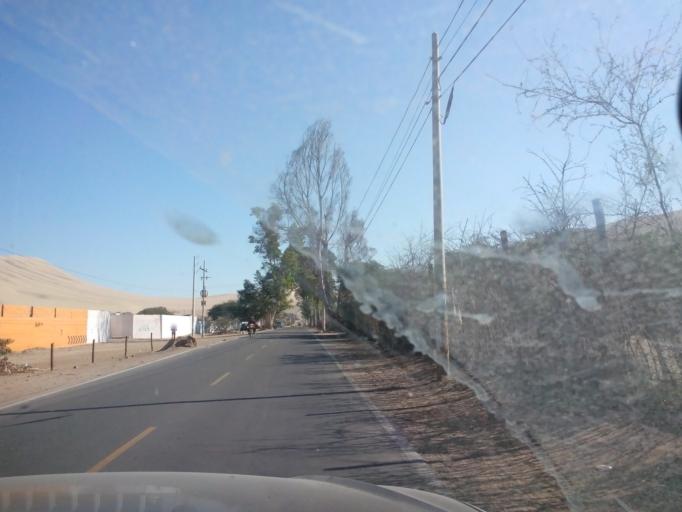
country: PE
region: Ica
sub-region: Provincia de Ica
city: Ica
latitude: -14.0826
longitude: -75.7516
